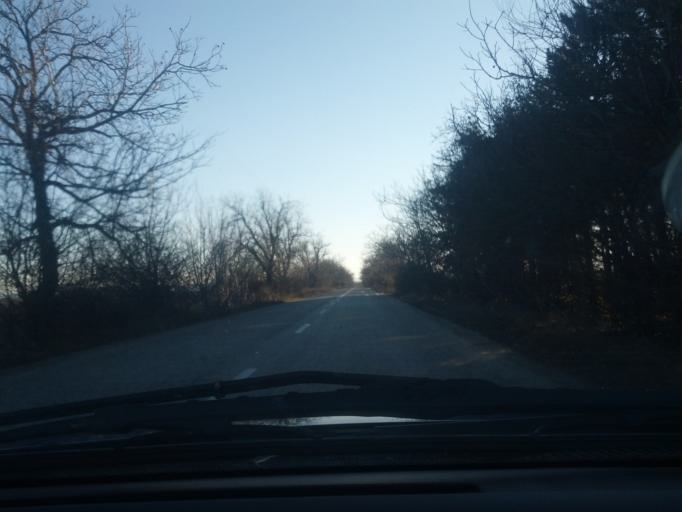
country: BG
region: Vratsa
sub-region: Obshtina Borovan
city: Borovan
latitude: 43.4879
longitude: 23.7956
